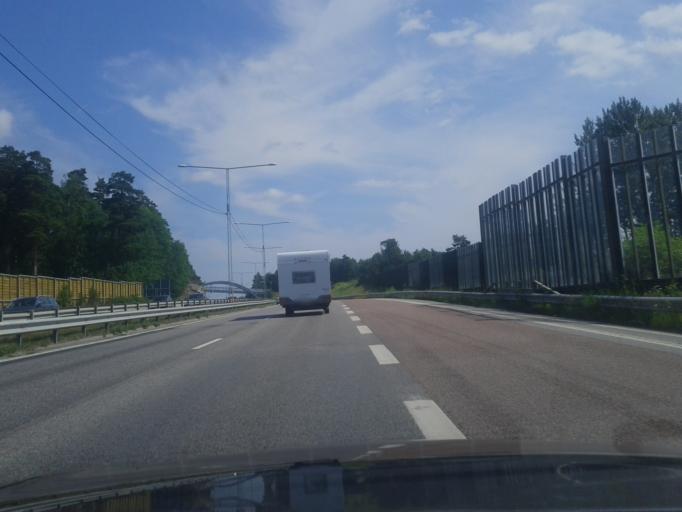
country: SE
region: Stockholm
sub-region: Taby Kommun
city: Taby
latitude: 59.4467
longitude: 18.1233
